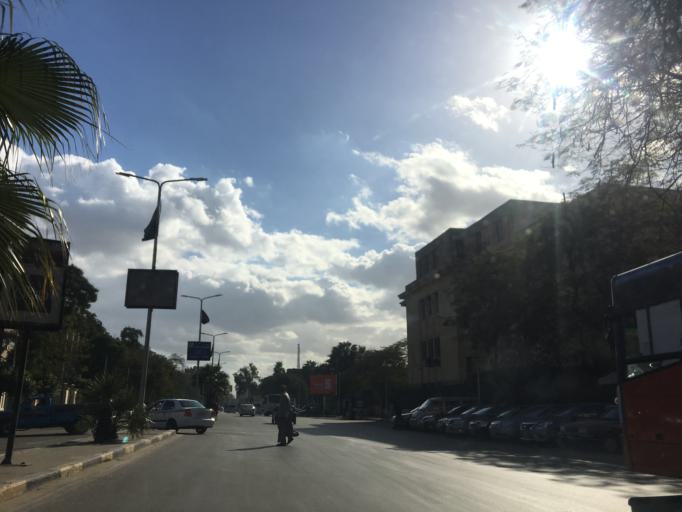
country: EG
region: Al Jizah
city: Al Jizah
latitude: 30.0251
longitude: 31.2109
